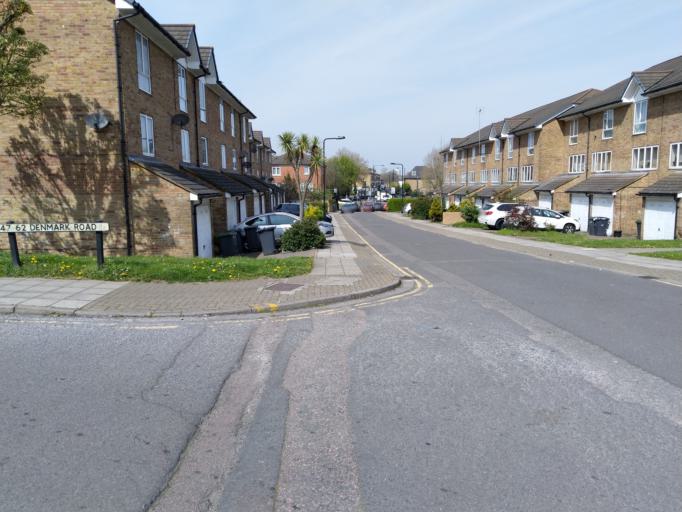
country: GB
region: England
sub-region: Greater London
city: Harringay
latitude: 51.5878
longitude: -0.1101
